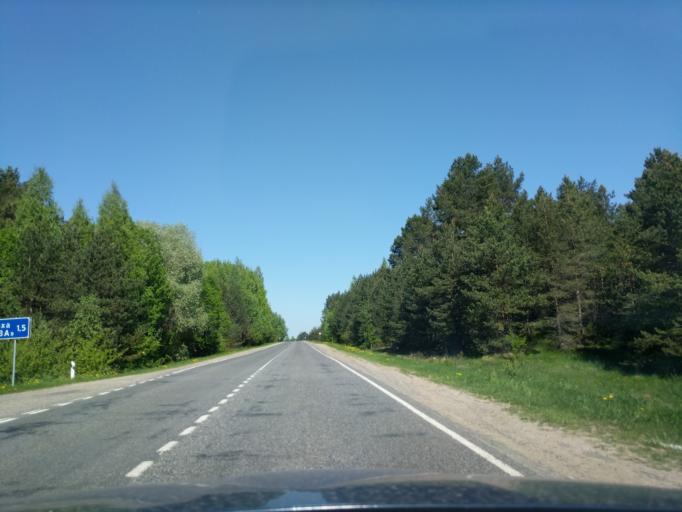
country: BY
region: Minsk
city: Myadzyel
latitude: 54.8981
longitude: 26.9047
